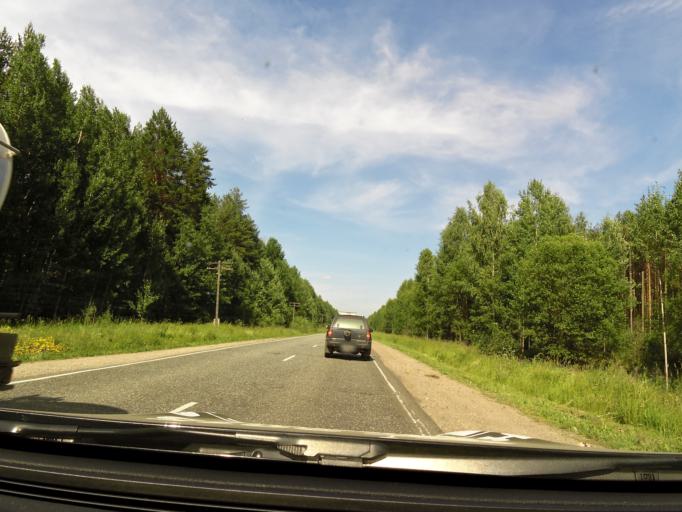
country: RU
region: Kirov
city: Belaya Kholunitsa
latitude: 58.7922
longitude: 50.5188
